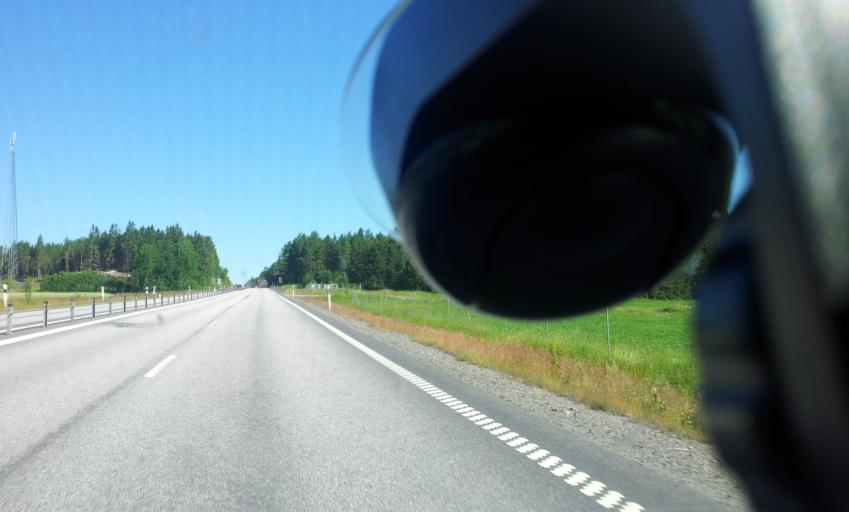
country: SE
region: OEstergoetland
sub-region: Valdemarsviks Kommun
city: Gusum
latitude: 58.3385
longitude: 16.4517
